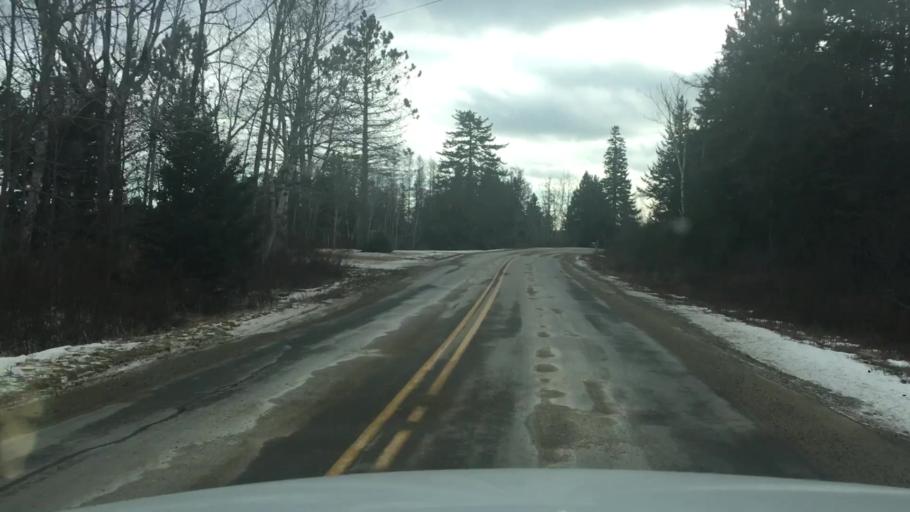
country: US
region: Maine
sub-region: Washington County
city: Machias
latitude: 44.6220
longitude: -67.4788
